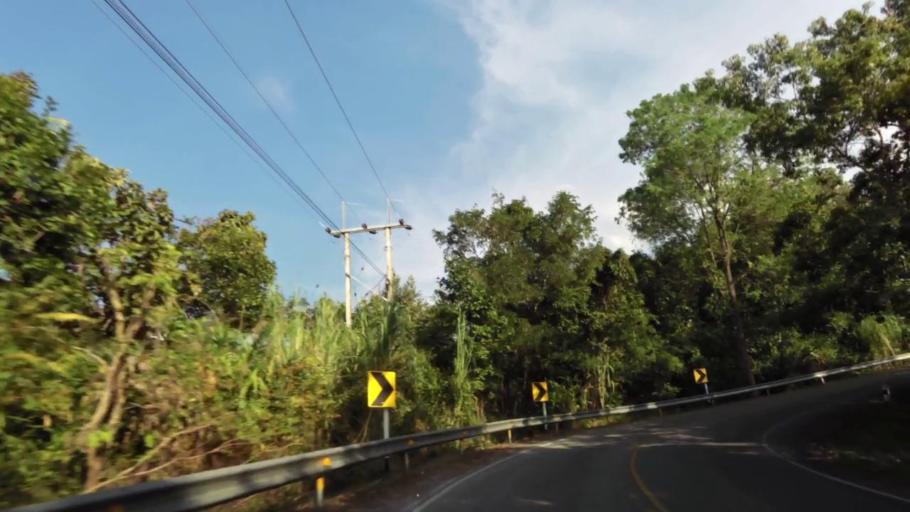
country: TH
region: Chiang Rai
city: Khun Tan
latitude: 19.8802
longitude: 100.3078
